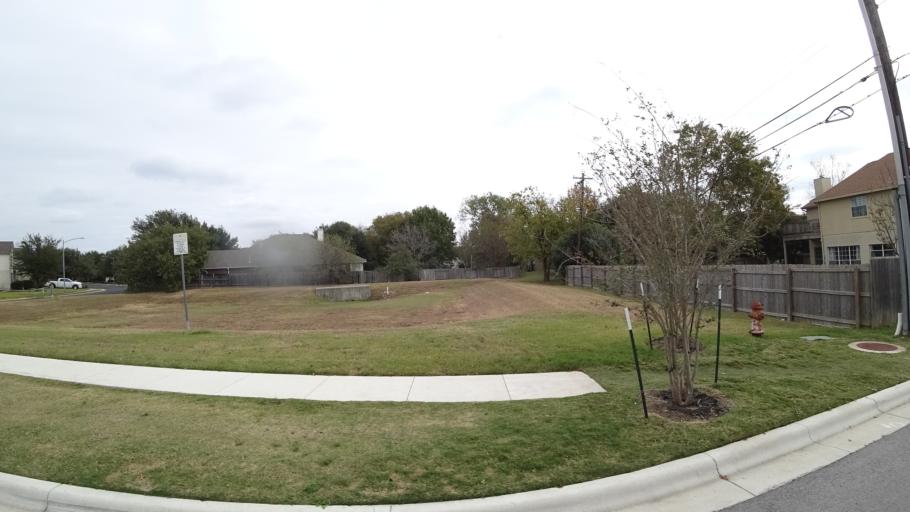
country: US
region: Texas
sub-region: Travis County
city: Wells Branch
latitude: 30.4261
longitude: -97.6963
